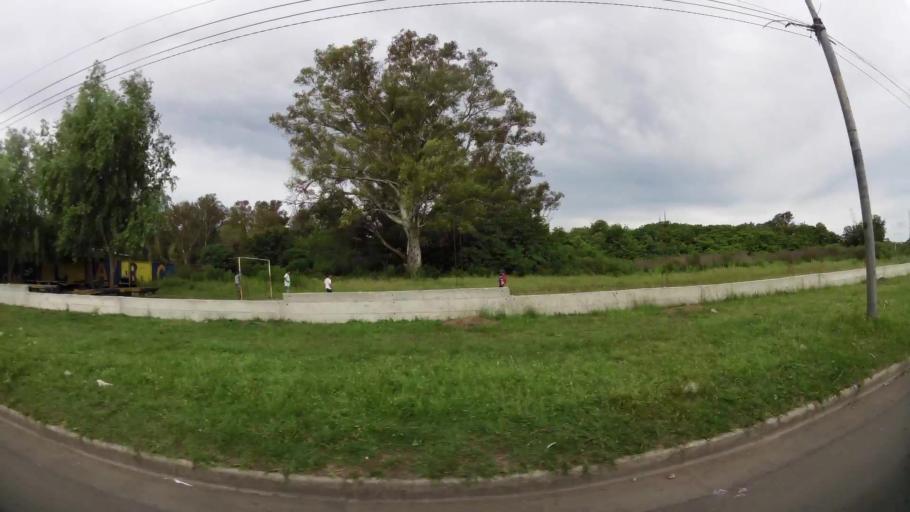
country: AR
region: Santa Fe
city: Gobernador Galvez
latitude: -32.9953
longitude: -60.6887
